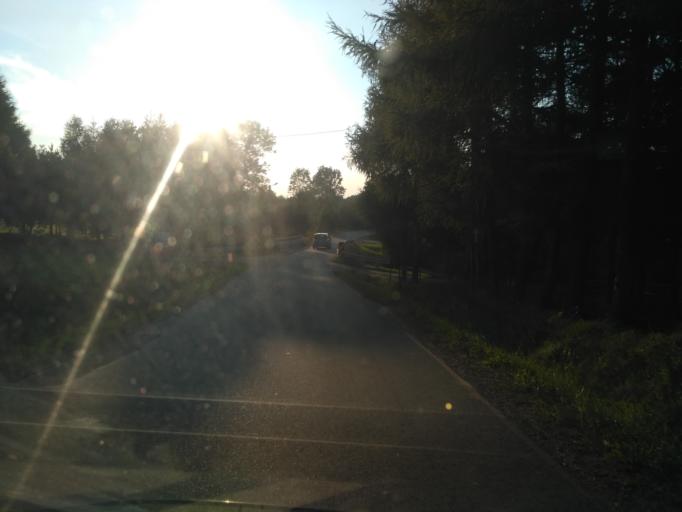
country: PL
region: Subcarpathian Voivodeship
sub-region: Powiat krosnienski
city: Korczyna
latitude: 49.7063
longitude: 21.8309
